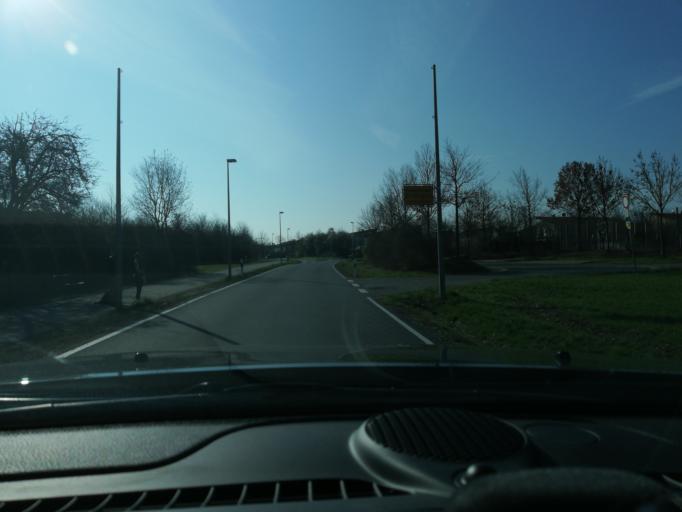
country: DE
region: Bavaria
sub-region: Regierungsbezirk Mittelfranken
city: Hessdorf
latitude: 49.5985
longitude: 10.9447
